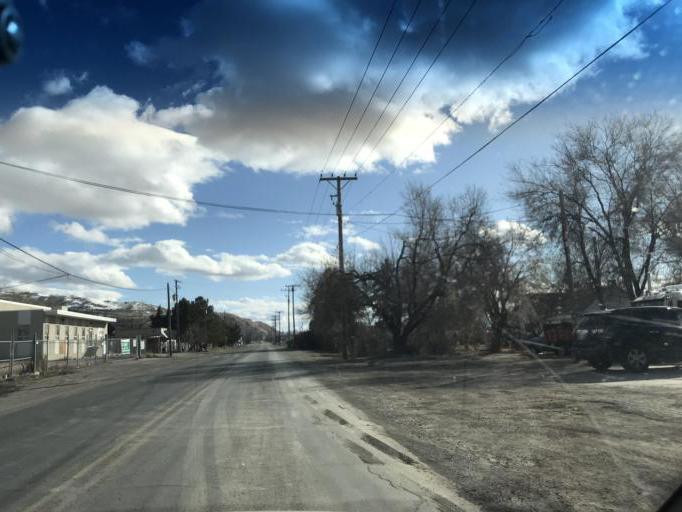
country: US
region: Utah
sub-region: Davis County
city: North Salt Lake
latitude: 40.8643
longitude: -111.9119
